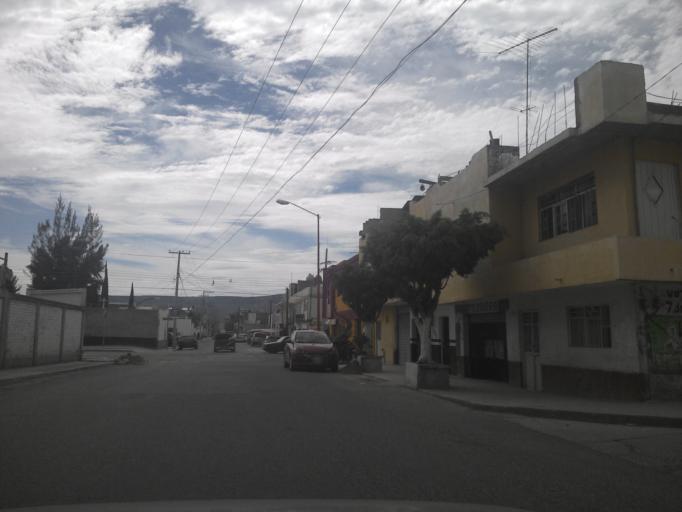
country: MX
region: Guanajuato
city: San Francisco del Rincon
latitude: 21.0103
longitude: -101.8514
